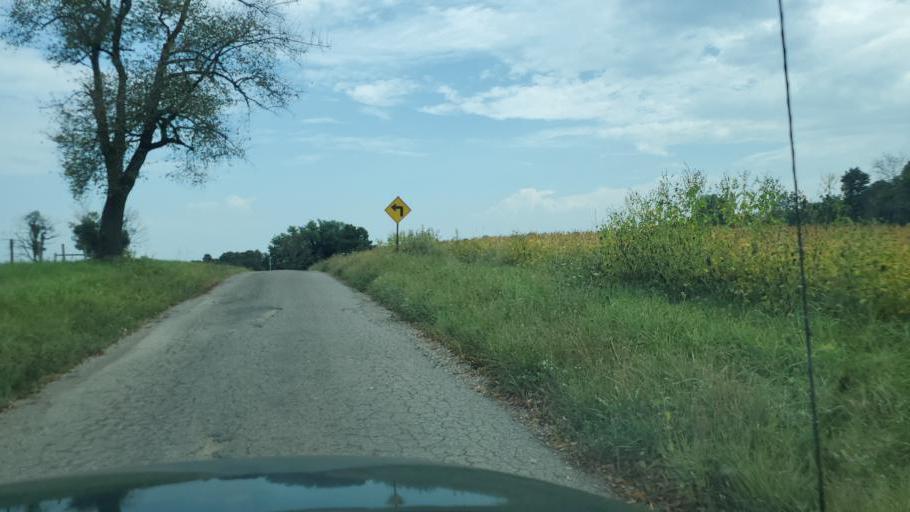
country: US
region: Ohio
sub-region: Muskingum County
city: Frazeysburg
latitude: 39.9839
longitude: -82.2082
